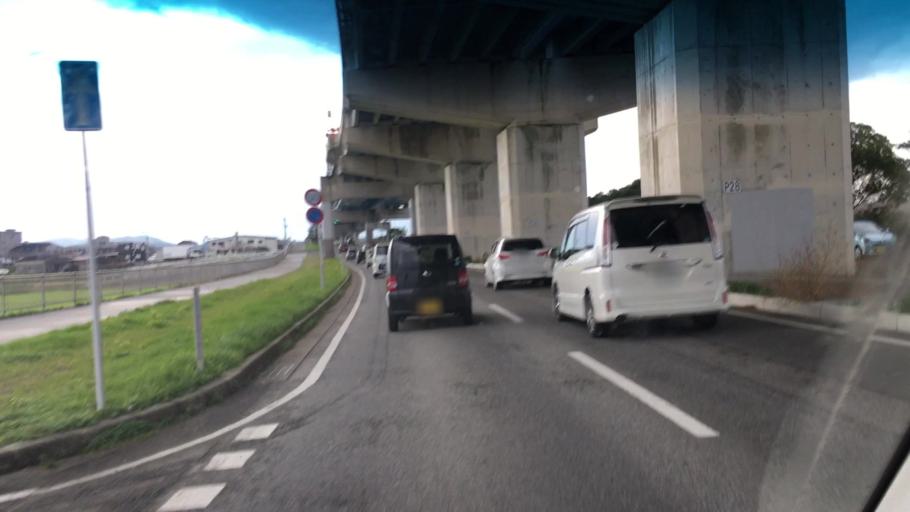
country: JP
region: Fukuoka
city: Maebaru-chuo
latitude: 33.5625
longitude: 130.2348
